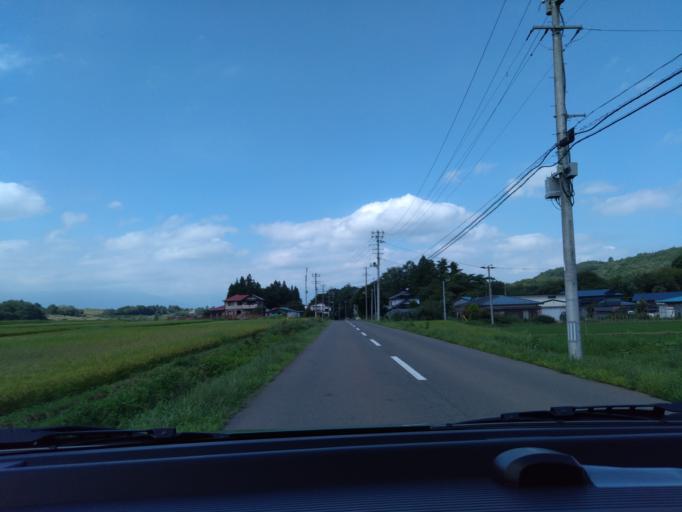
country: JP
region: Iwate
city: Shizukuishi
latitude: 39.6505
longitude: 140.9928
